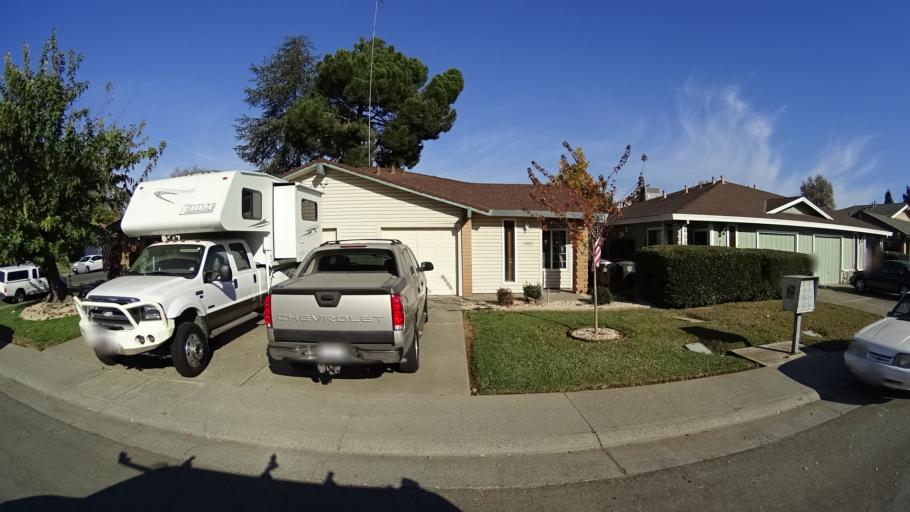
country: US
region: California
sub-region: Sacramento County
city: Citrus Heights
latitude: 38.6919
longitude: -121.2936
